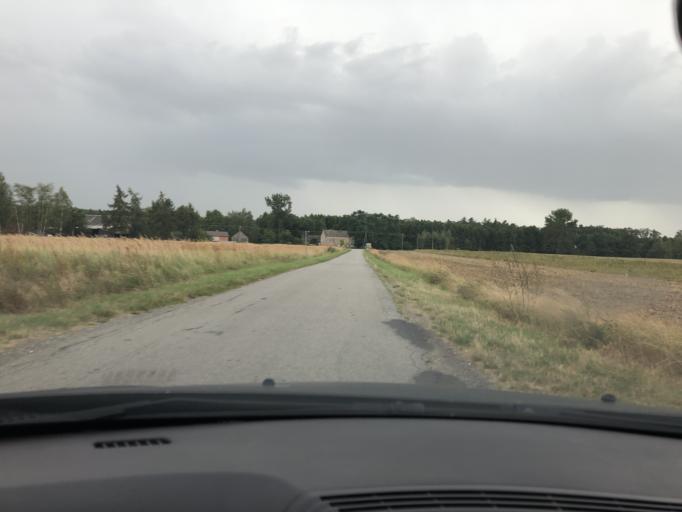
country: PL
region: Lodz Voivodeship
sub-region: Powiat wieruszowski
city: Czastary
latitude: 51.2447
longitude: 18.2773
